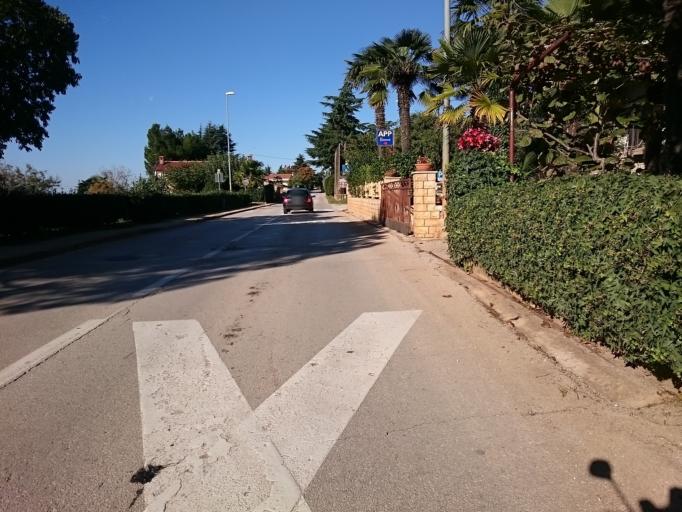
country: HR
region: Istarska
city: Novigrad
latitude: 45.3595
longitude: 13.5550
